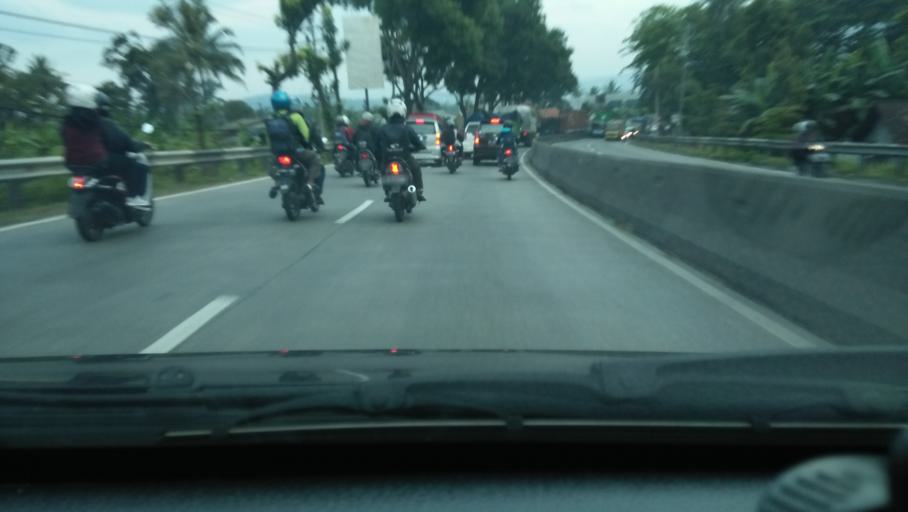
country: ID
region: Central Java
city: Ambarawa
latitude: -7.2389
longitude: 110.4345
